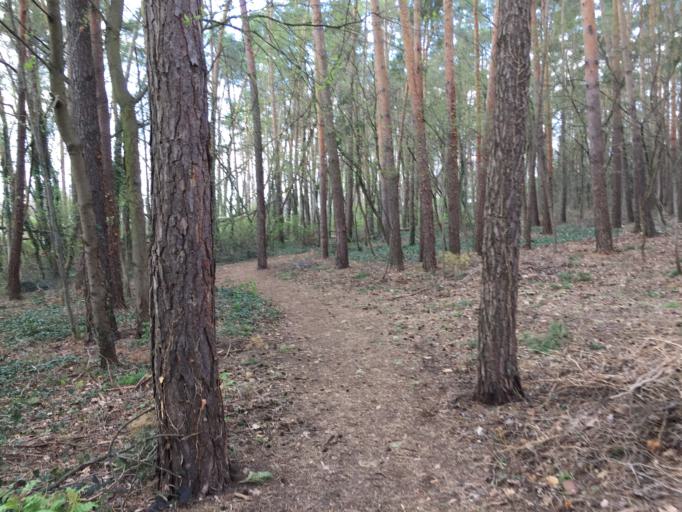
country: DE
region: Bavaria
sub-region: Regierungsbezirk Mittelfranken
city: Erlangen
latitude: 49.5626
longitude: 10.9980
